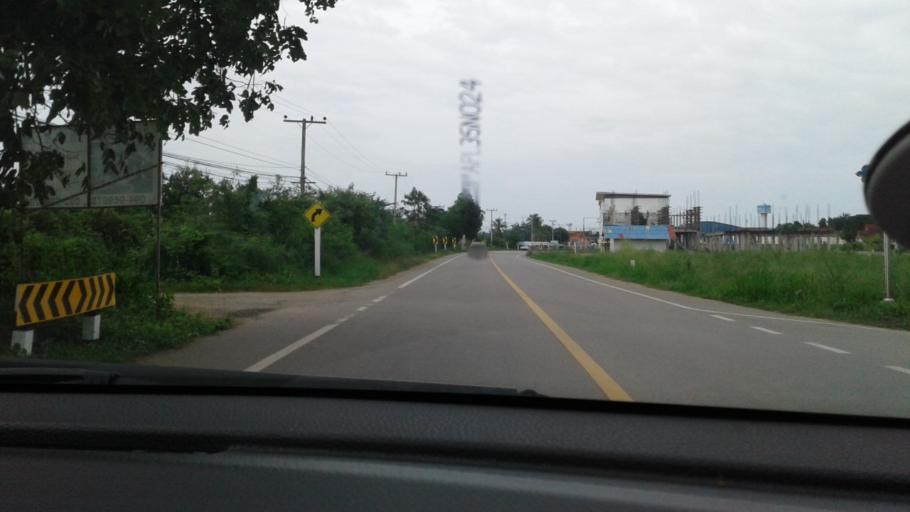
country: TH
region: Prachuap Khiri Khan
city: Pran Buri
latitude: 12.3868
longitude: 99.9846
